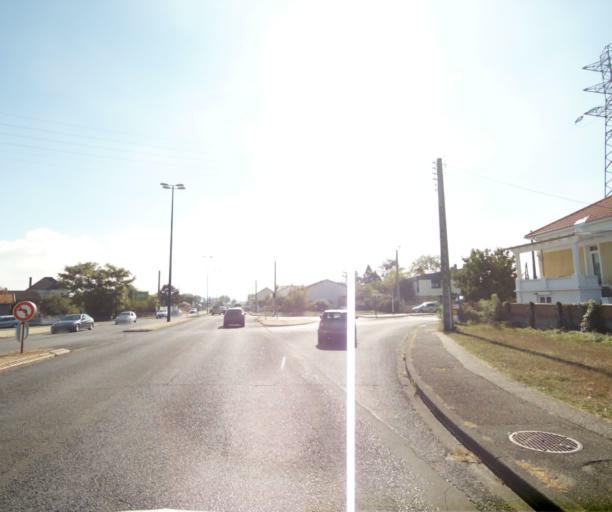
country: FR
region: Auvergne
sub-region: Departement du Puy-de-Dome
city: Aubiere
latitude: 45.7601
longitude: 3.1220
